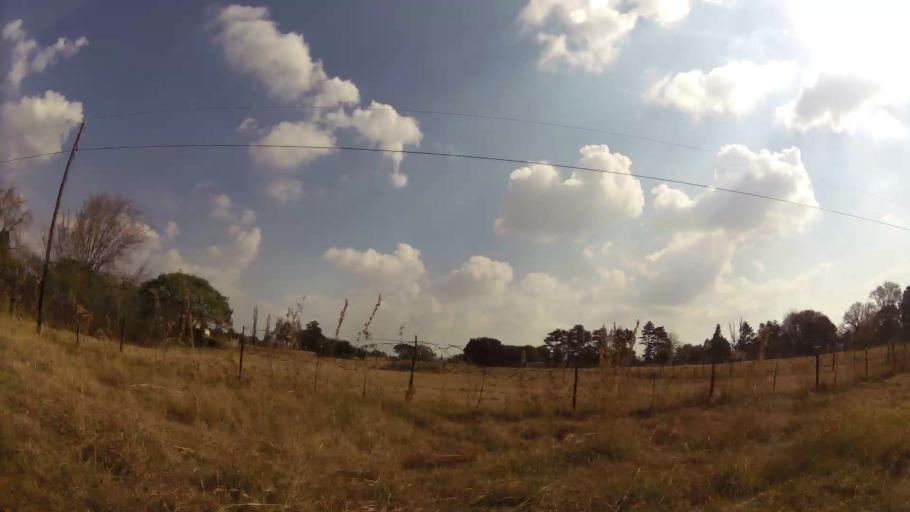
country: ZA
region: Mpumalanga
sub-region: Nkangala District Municipality
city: Delmas
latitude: -26.1658
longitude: 28.5474
